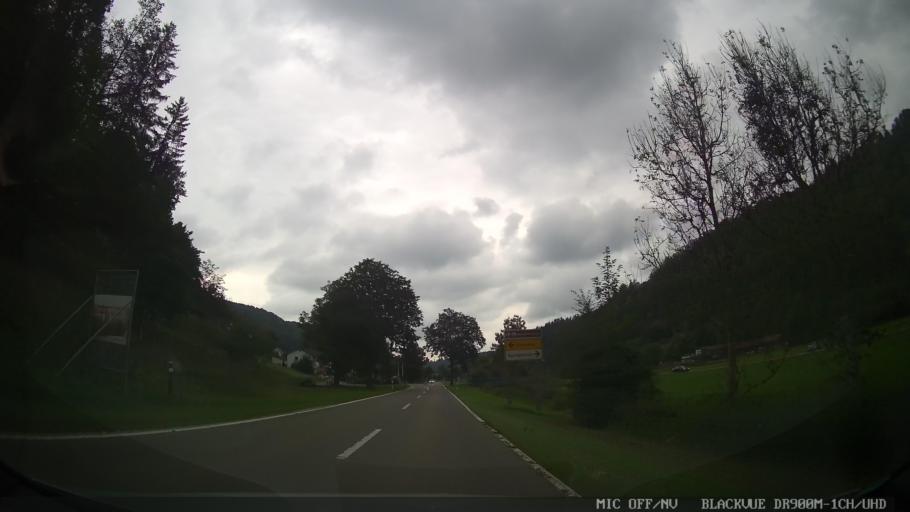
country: DE
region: Baden-Wuerttemberg
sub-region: Freiburg Region
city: Barenthal
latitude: 48.0793
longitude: 8.9258
